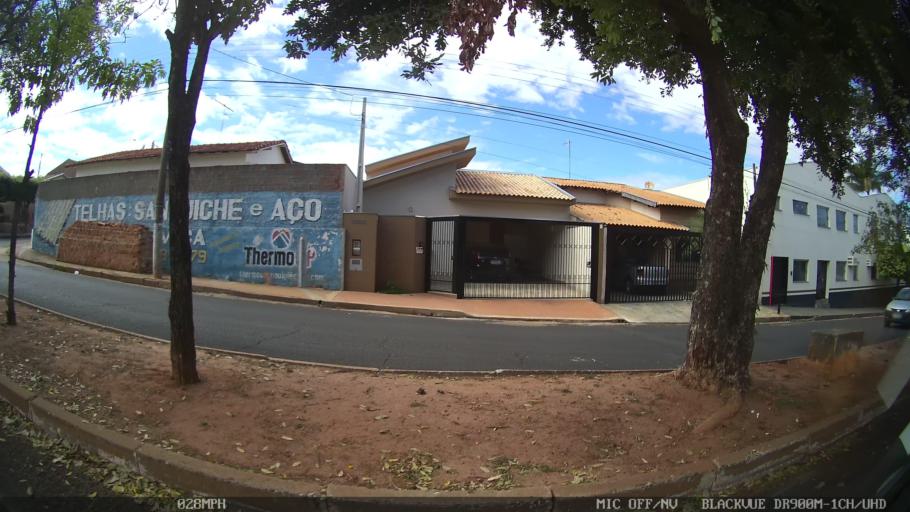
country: BR
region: Sao Paulo
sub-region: Bady Bassitt
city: Bady Bassitt
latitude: -20.8206
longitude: -49.5234
